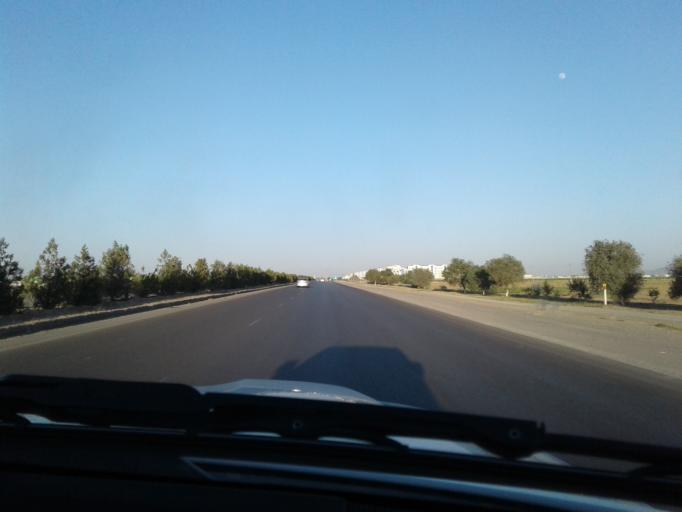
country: TM
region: Ahal
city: Abadan
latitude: 38.1690
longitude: 57.9217
